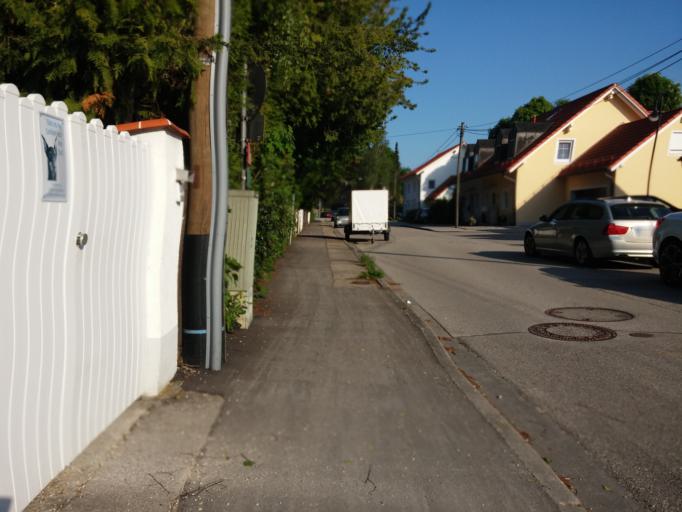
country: DE
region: Bavaria
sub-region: Upper Bavaria
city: Vaterstetten
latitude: 48.0994
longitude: 11.7572
